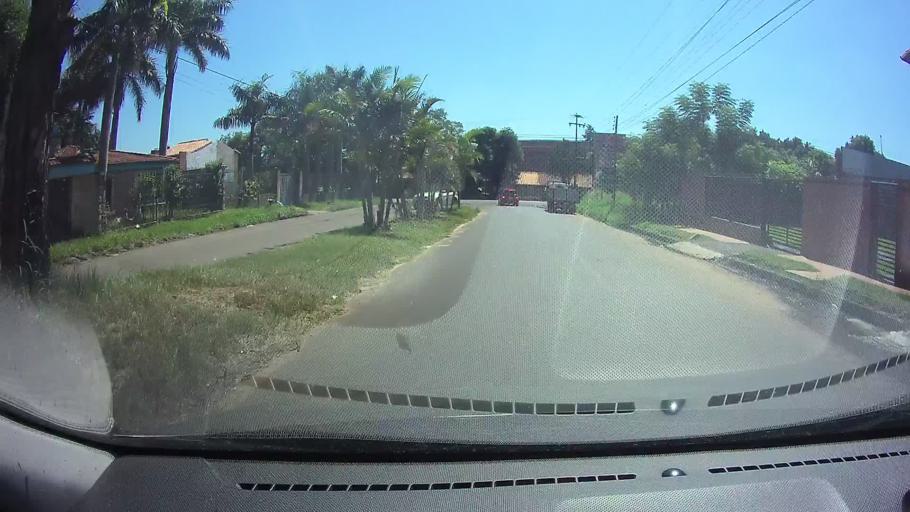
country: PY
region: Central
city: Fernando de la Mora
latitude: -25.2854
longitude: -57.5195
